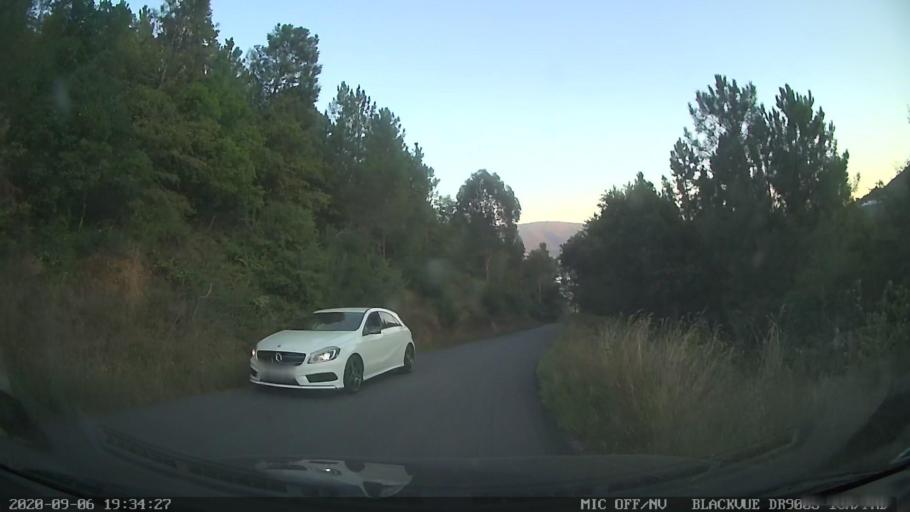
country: PT
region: Vila Real
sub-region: Mesao Frio
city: Mesao Frio
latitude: 41.1715
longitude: -7.8956
